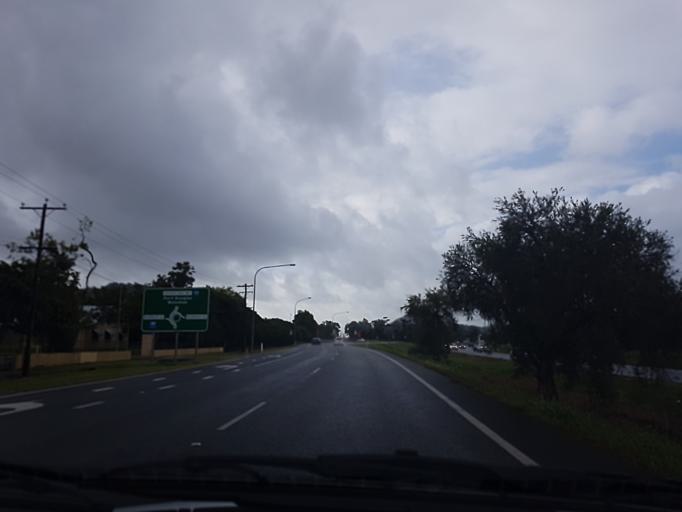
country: AU
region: Queensland
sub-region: Cairns
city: Yorkeys Knob
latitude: -16.8240
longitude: 145.6924
